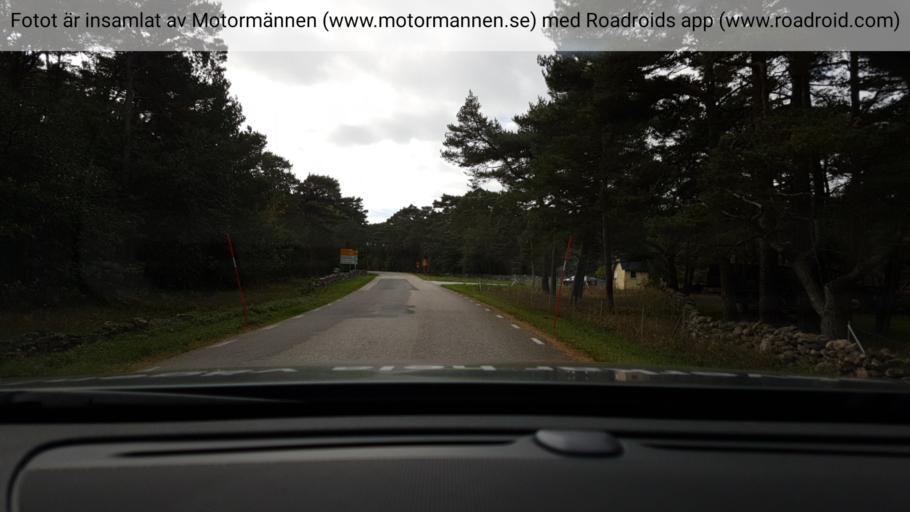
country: SE
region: Gotland
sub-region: Gotland
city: Hemse
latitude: 56.9527
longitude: 18.2105
